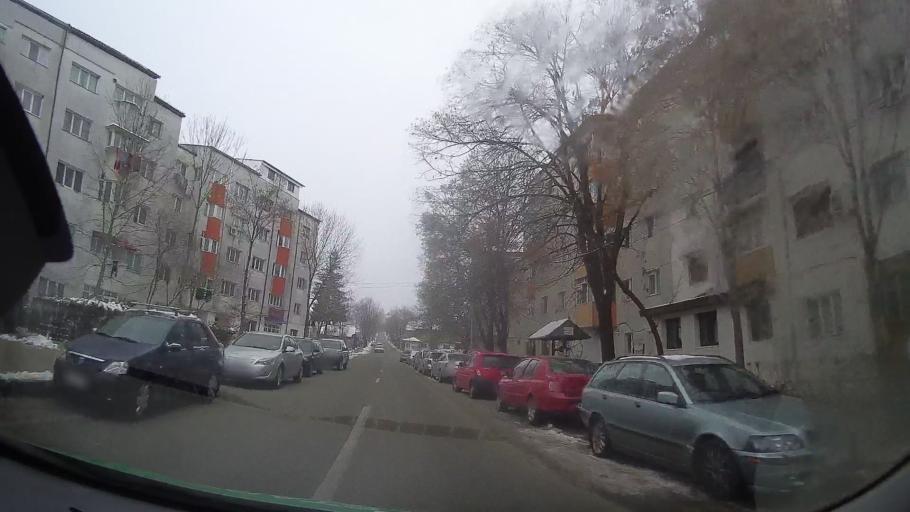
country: RO
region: Vaslui
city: Vaslui
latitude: 46.6506
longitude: 27.7331
